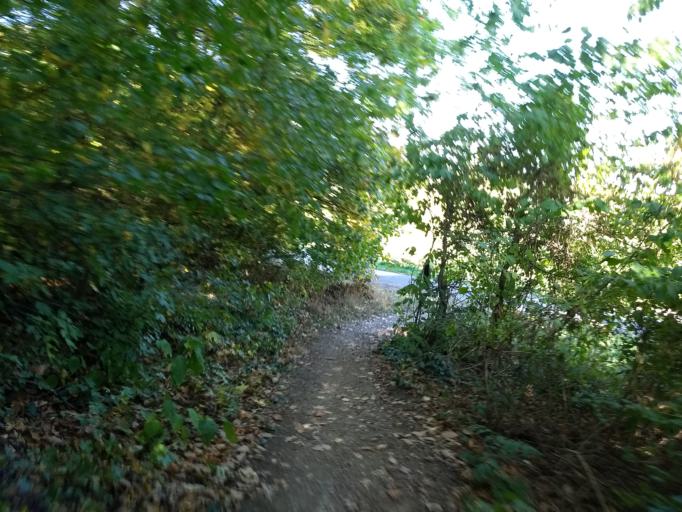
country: AT
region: Lower Austria
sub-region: Politischer Bezirk Modling
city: Giesshubl
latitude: 48.1074
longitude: 16.2407
